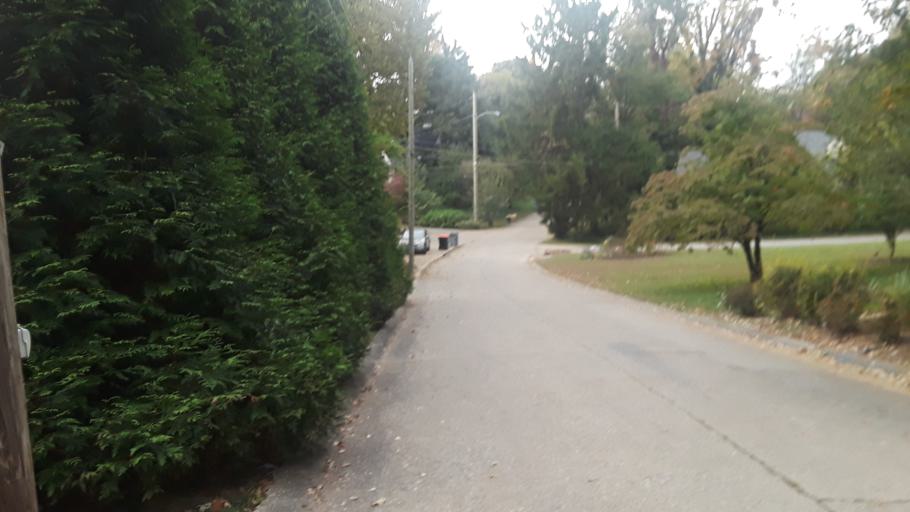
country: US
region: Kentucky
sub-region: Jefferson County
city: Saint Matthews
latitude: 38.2462
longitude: -85.6940
